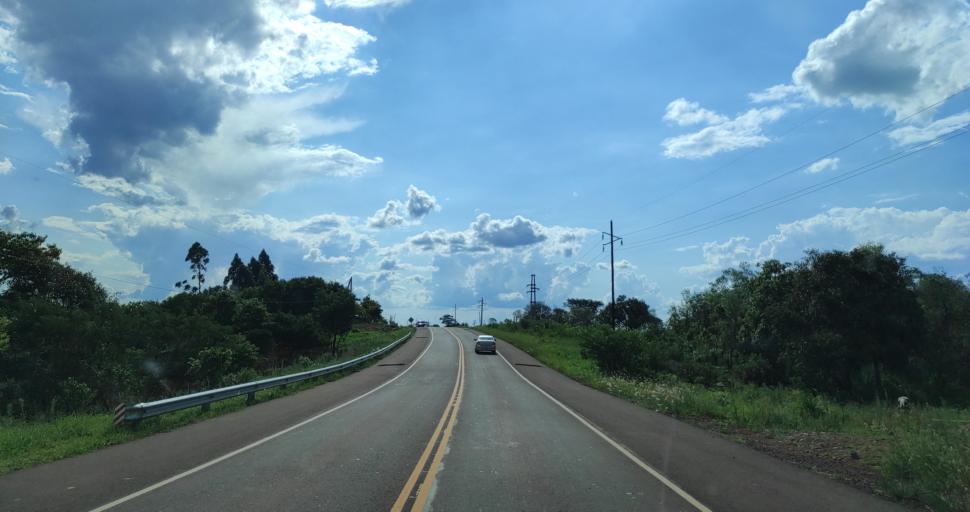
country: AR
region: Misiones
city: Bernardo de Irigoyen
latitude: -26.2988
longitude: -53.8069
